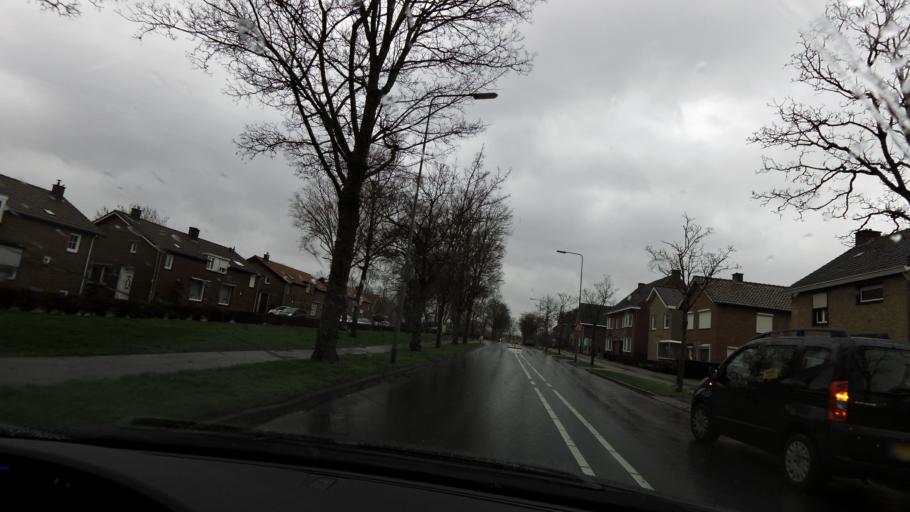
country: NL
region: Limburg
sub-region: Gemeente Stein
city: Elsloo
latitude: 50.9585
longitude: 5.7715
